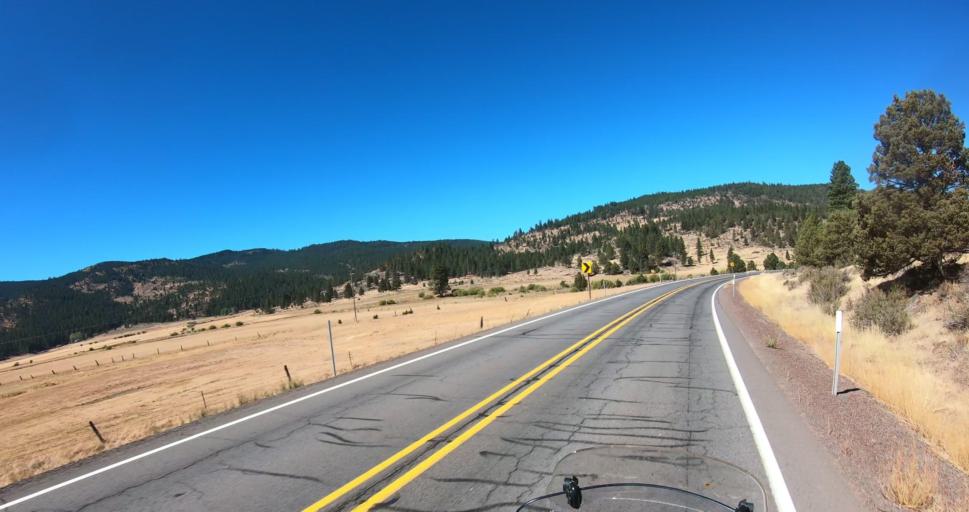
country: US
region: Oregon
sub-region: Lake County
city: Lakeview
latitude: 42.3829
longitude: -120.3063
